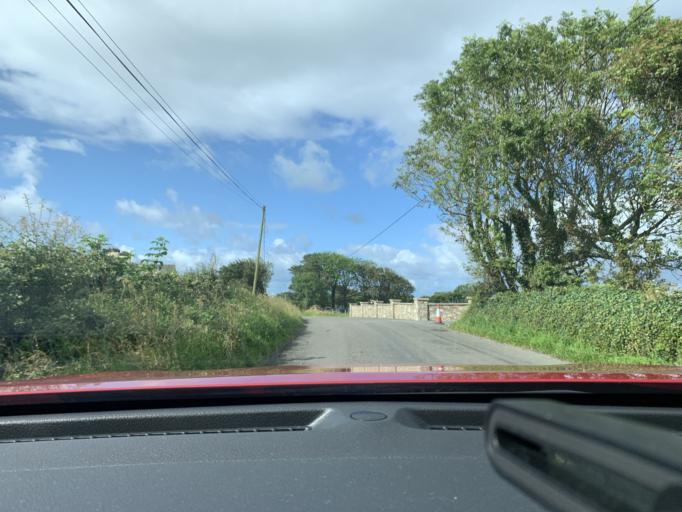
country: IE
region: Connaught
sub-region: Sligo
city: Strandhill
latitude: 54.3664
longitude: -8.5998
